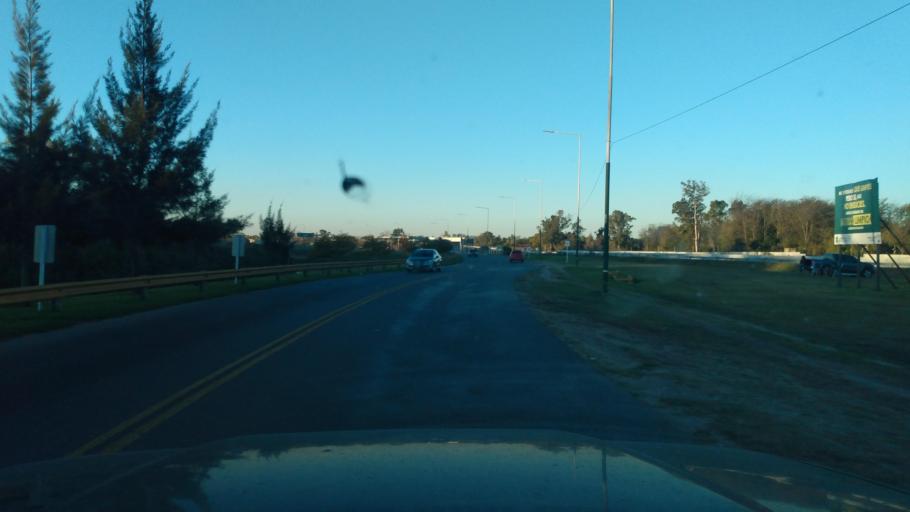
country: AR
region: Buenos Aires
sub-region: Partido de Merlo
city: Merlo
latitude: -34.6352
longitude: -58.7292
